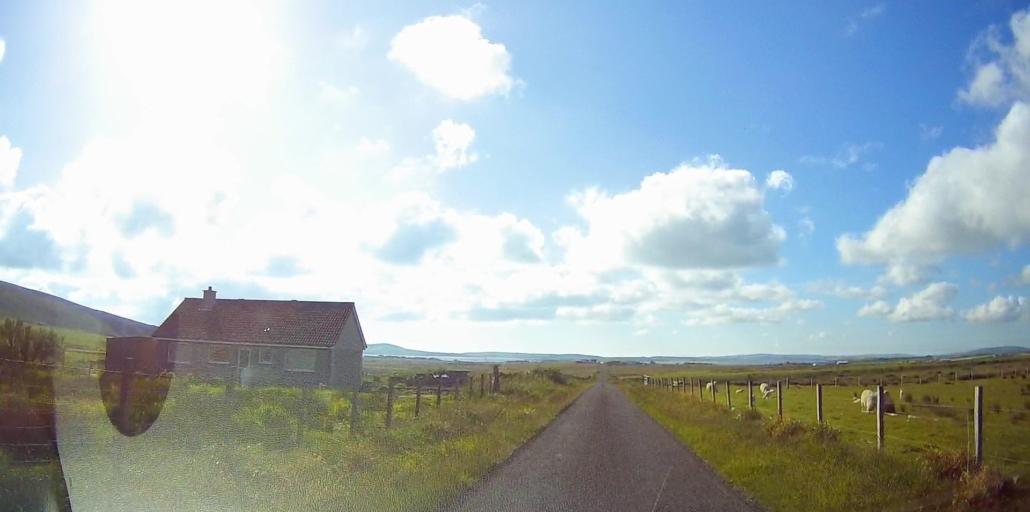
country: GB
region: Scotland
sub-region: Orkney Islands
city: Stromness
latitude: 58.9801
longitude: -3.1734
